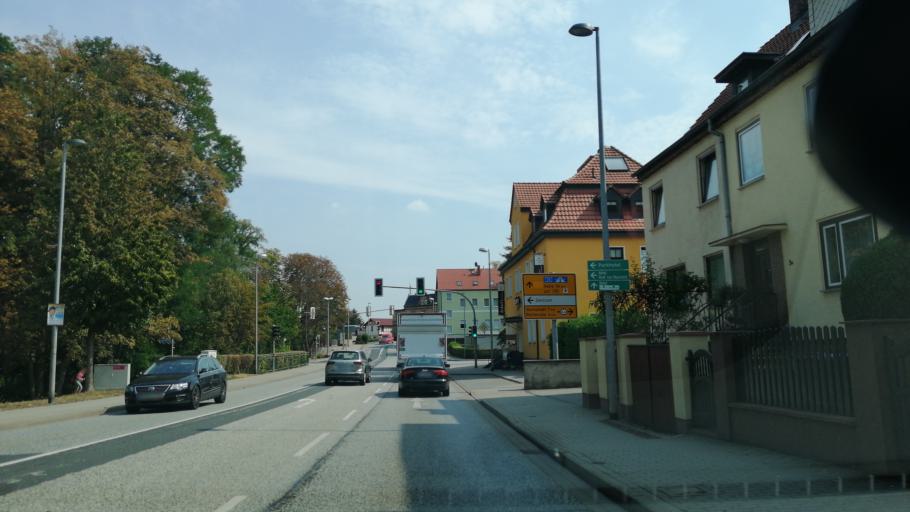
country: DE
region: Saxony-Anhalt
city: Wimmelburg
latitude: 51.5208
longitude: 11.5472
